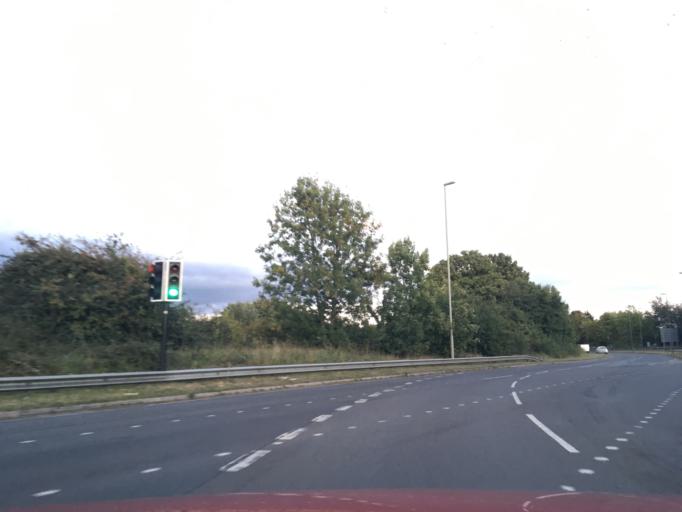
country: GB
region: England
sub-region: Gloucestershire
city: Barnwood
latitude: 51.8664
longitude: -2.1960
